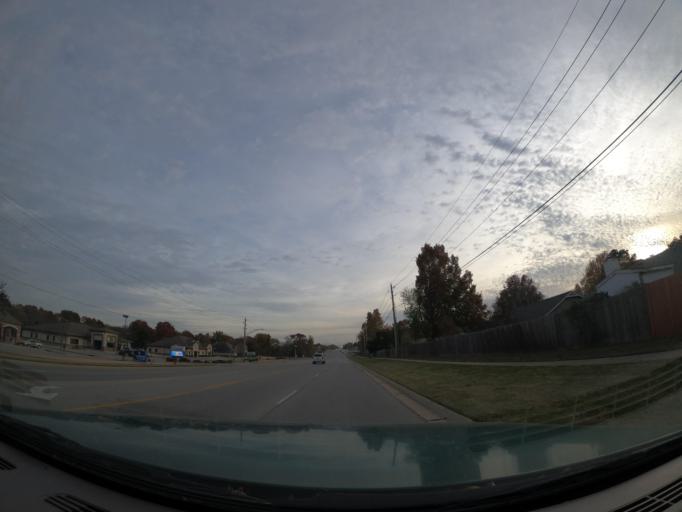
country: US
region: Oklahoma
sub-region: Tulsa County
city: Broken Arrow
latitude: 36.0507
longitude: -95.8154
